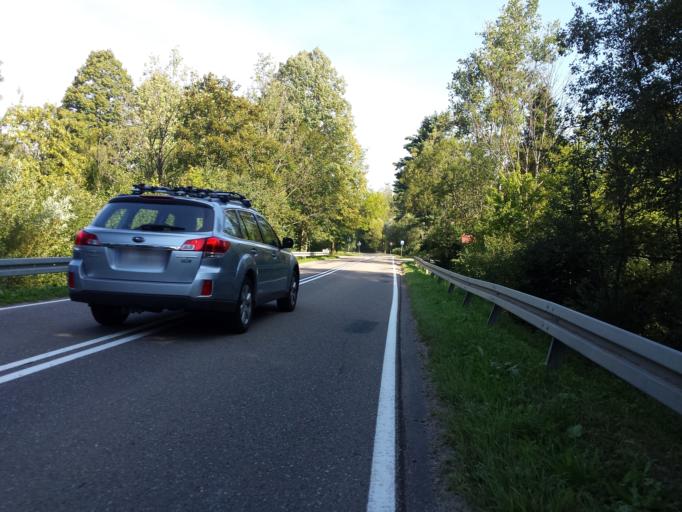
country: PL
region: Subcarpathian Voivodeship
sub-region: Powiat leski
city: Baligrod
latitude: 49.3047
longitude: 22.2768
